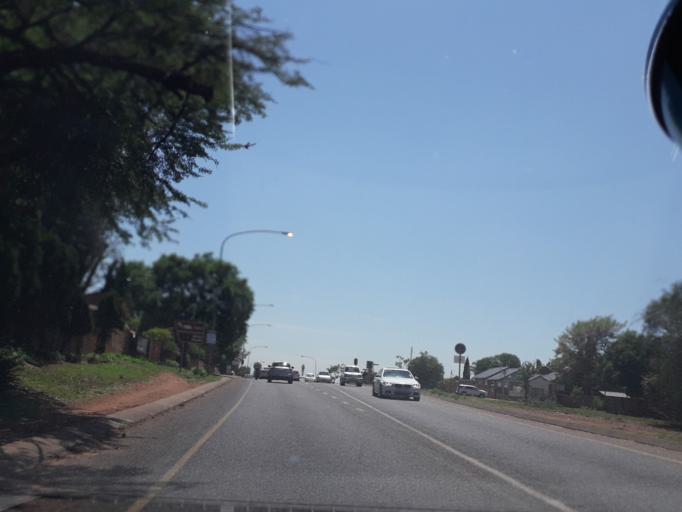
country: ZA
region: Gauteng
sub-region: City of Tshwane Metropolitan Municipality
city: Centurion
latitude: -25.8674
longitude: 28.1815
